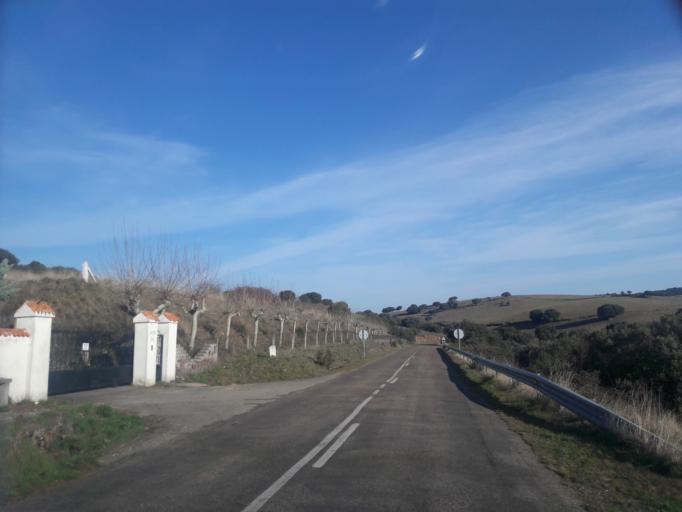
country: ES
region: Castille and Leon
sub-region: Provincia de Salamanca
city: Salvatierra de Tormes
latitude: 40.5892
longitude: -5.6046
